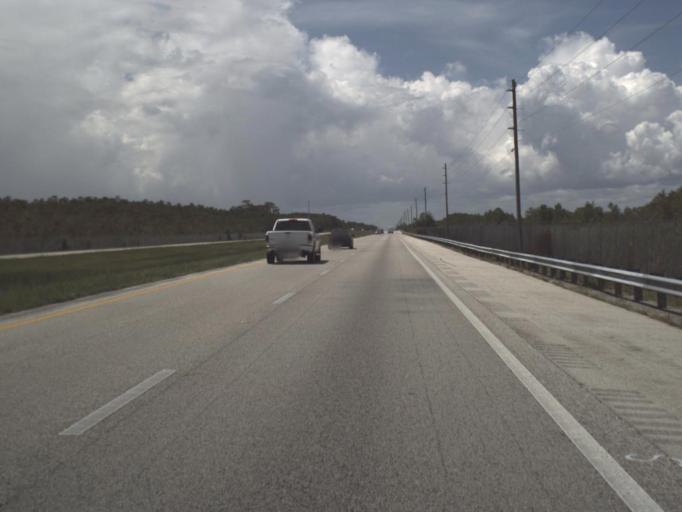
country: US
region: Florida
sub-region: Collier County
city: Immokalee
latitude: 26.1681
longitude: -81.1290
